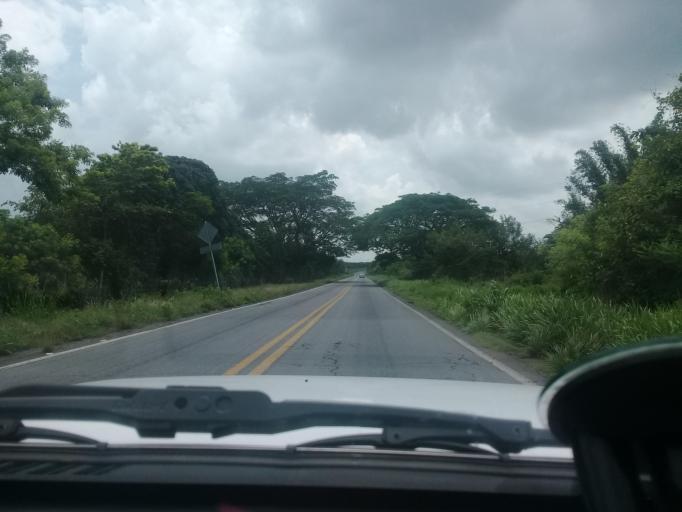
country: MX
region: Veracruz
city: Paso de Ovejas
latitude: 19.2915
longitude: -96.4541
